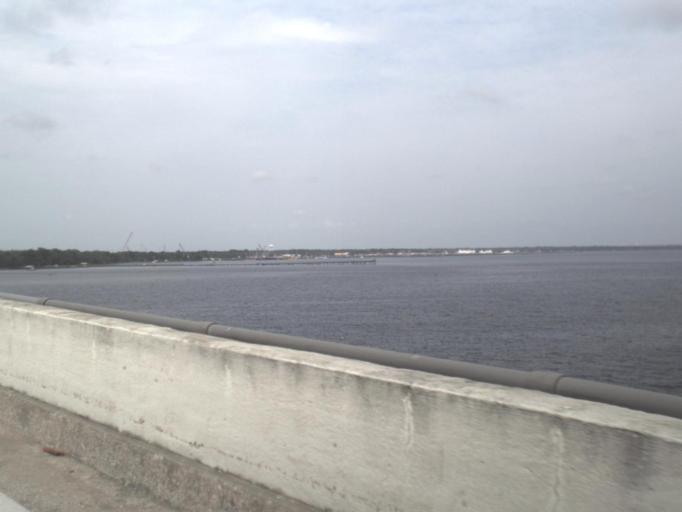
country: US
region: Florida
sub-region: Clay County
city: Green Cove Springs
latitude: 29.9832
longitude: -81.6210
